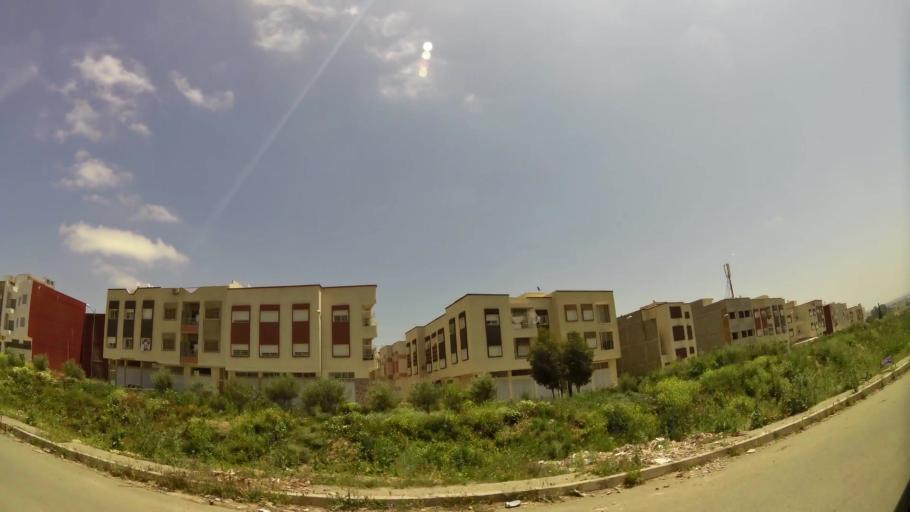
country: MA
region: Fes-Boulemane
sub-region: Fes
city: Fes
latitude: 34.0505
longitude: -5.0447
